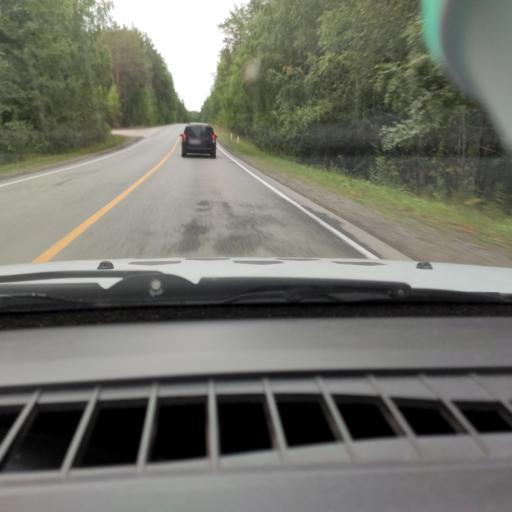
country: RU
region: Chelyabinsk
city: Kyshtym
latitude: 55.7644
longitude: 60.5630
